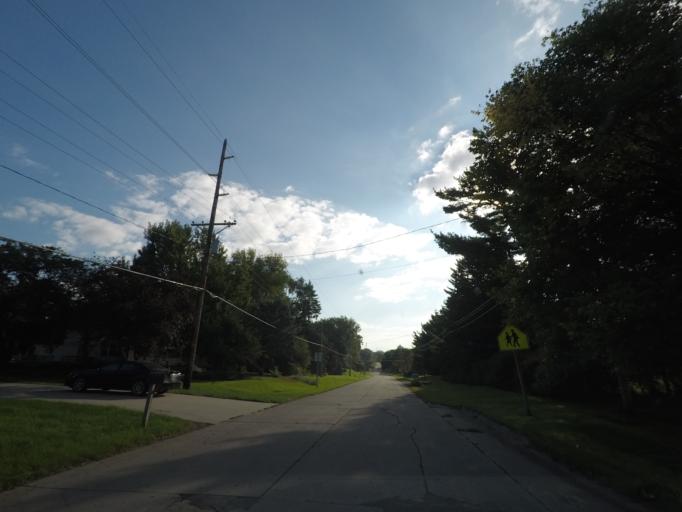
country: US
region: Iowa
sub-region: Story County
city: Nevada
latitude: 42.0155
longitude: -93.4613
